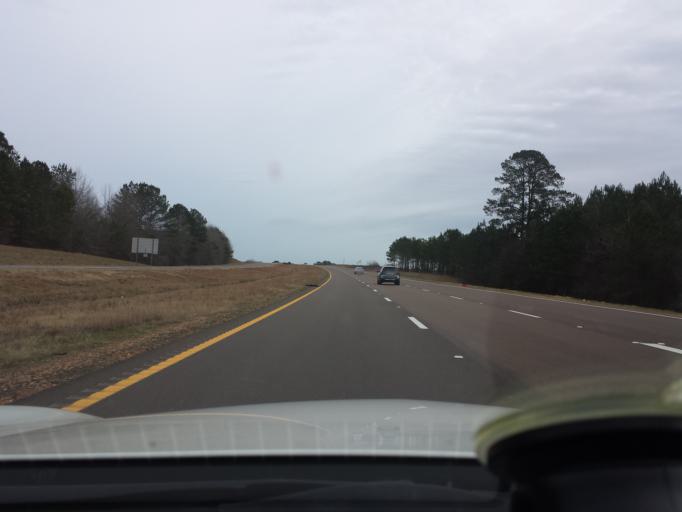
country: US
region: Mississippi
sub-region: Leake County
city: Carthage
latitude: 32.7709
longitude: -89.5358
